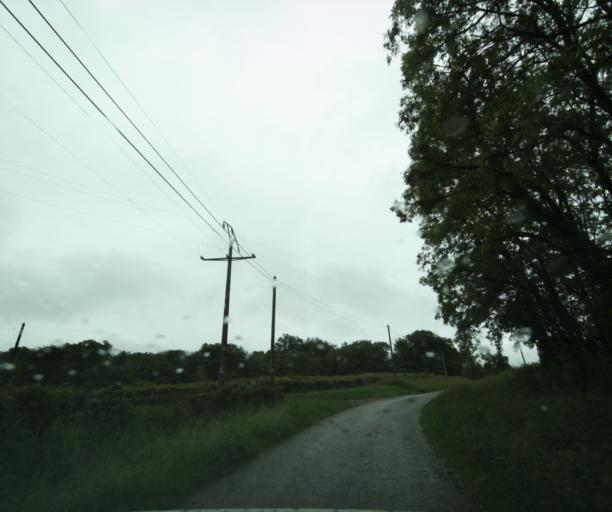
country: FR
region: Bourgogne
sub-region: Departement de Saone-et-Loire
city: Charolles
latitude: 46.4823
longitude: 4.2930
